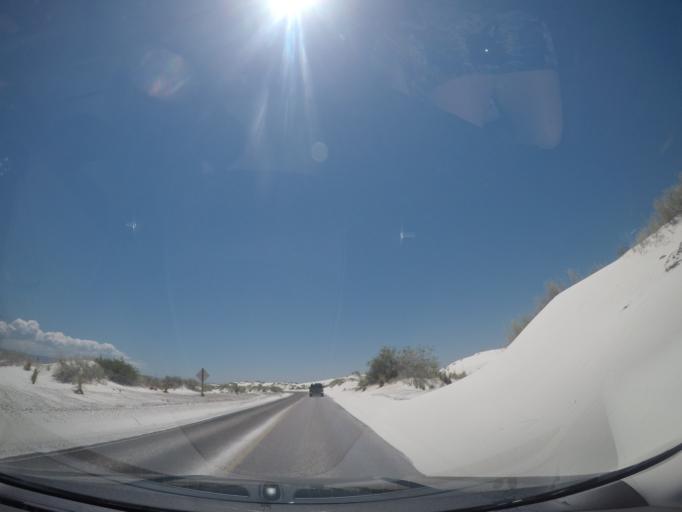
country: US
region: New Mexico
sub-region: Otero County
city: Holloman Air Force Base
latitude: 32.7950
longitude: -106.2430
